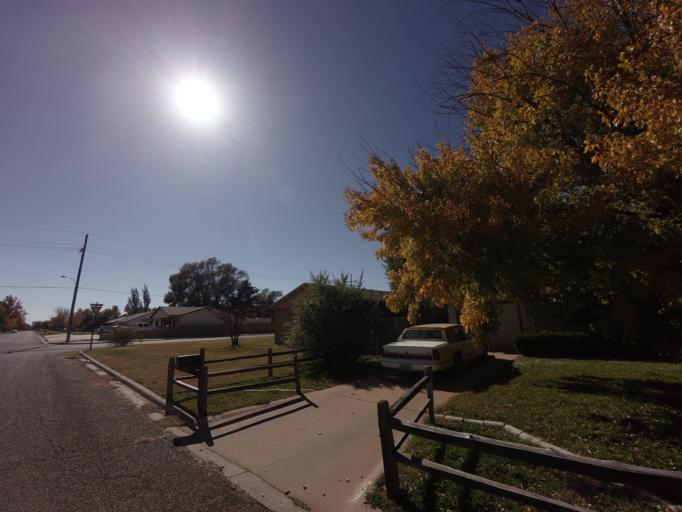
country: US
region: New Mexico
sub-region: Curry County
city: Clovis
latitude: 34.4305
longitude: -103.1979
